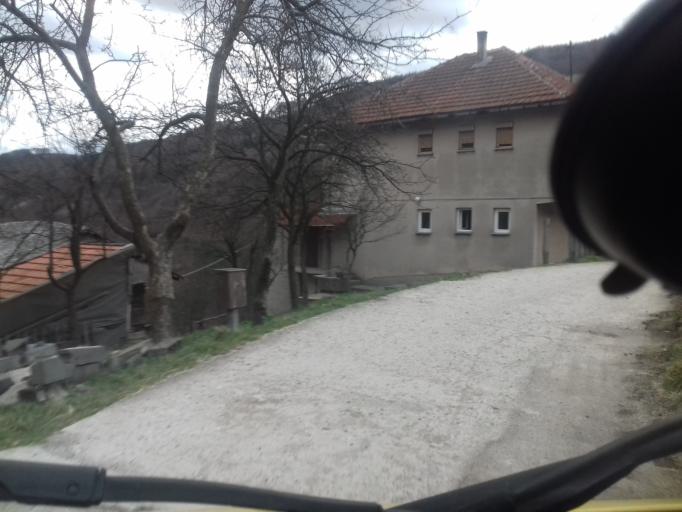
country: BA
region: Federation of Bosnia and Herzegovina
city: Zenica
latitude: 44.2382
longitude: 18.0081
